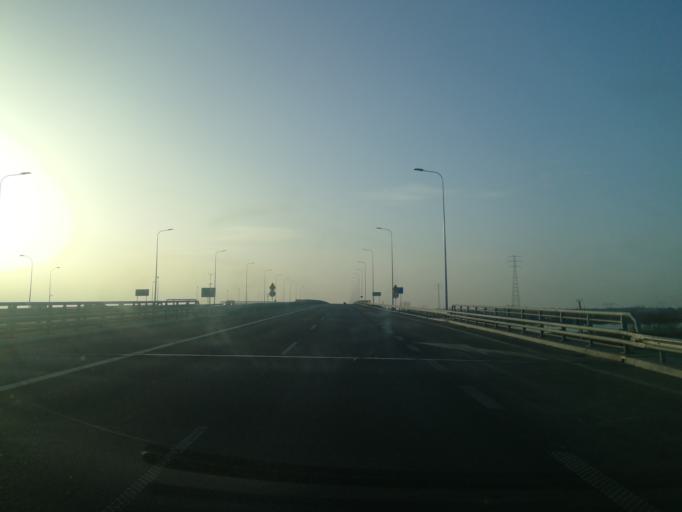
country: PL
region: Pomeranian Voivodeship
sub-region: Powiat nowodworski
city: Ostaszewo
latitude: 54.2566
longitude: 18.9523
